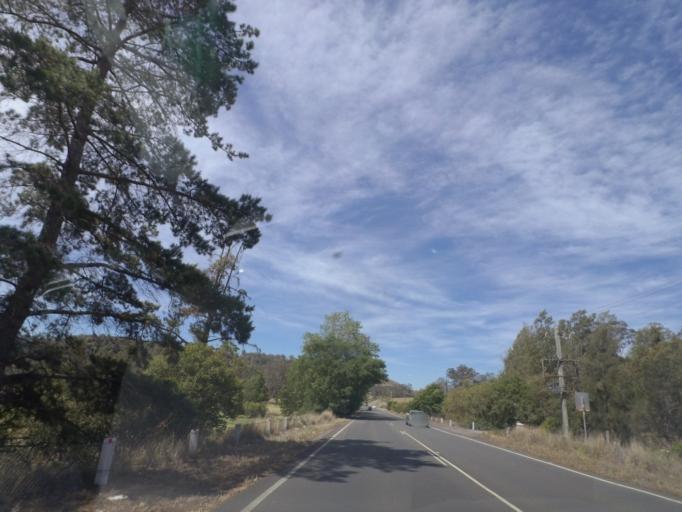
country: AU
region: New South Wales
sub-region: Wollondilly
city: Picton
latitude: -34.1666
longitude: 150.6294
